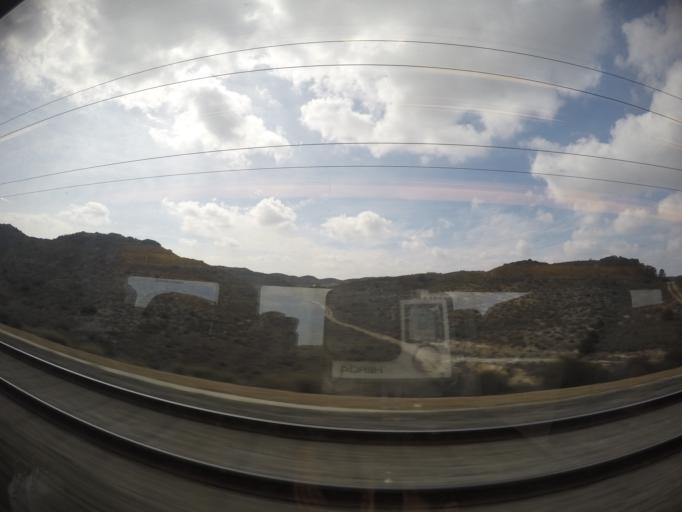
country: ES
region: Aragon
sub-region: Provincia de Huesca
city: Castejon de Monegros
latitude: 41.5310
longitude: -0.3286
